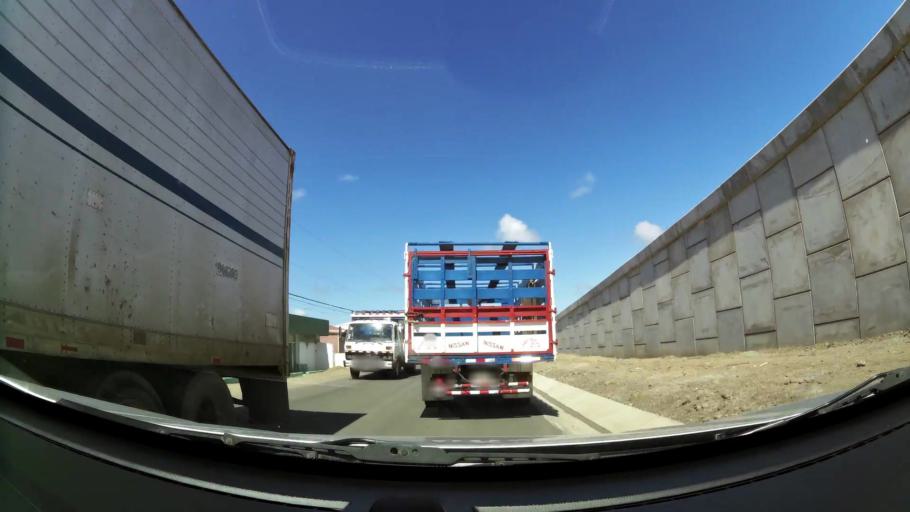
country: CR
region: Guanacaste
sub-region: Canton de Canas
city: Canas
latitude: 10.4287
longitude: -85.0953
